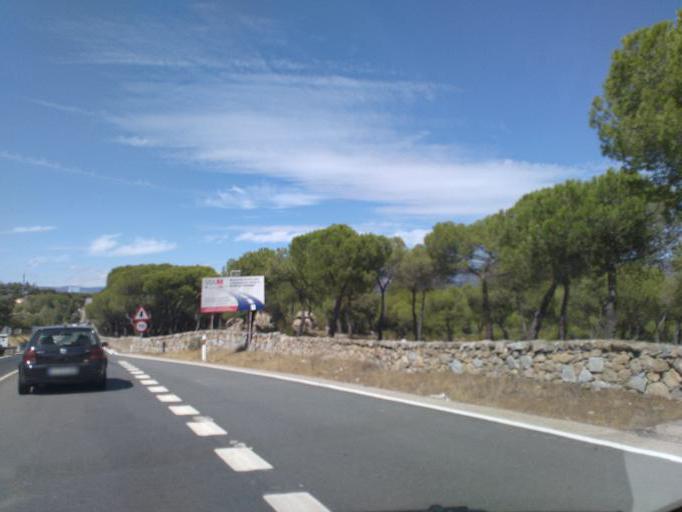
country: ES
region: Madrid
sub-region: Provincia de Madrid
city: Torrelodones
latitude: 40.5557
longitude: -3.9623
